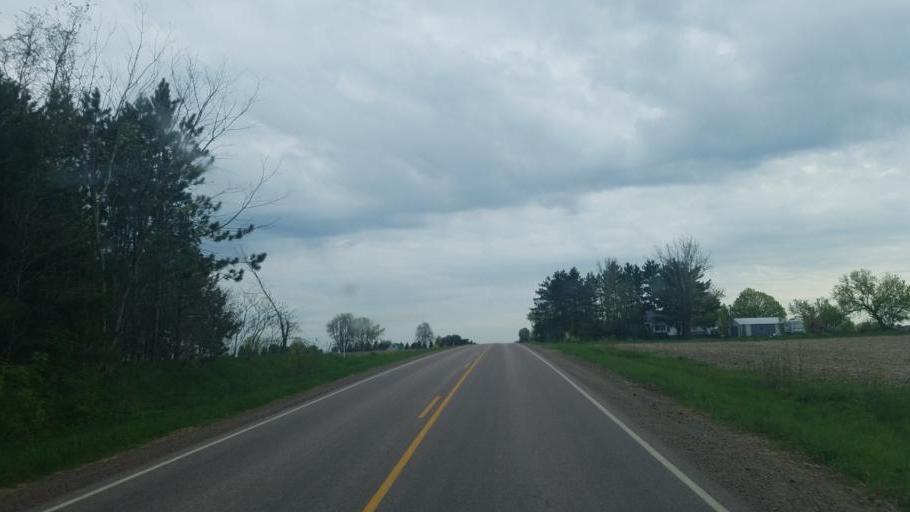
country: US
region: Wisconsin
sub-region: Wood County
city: Marshfield
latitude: 44.5915
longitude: -90.2989
